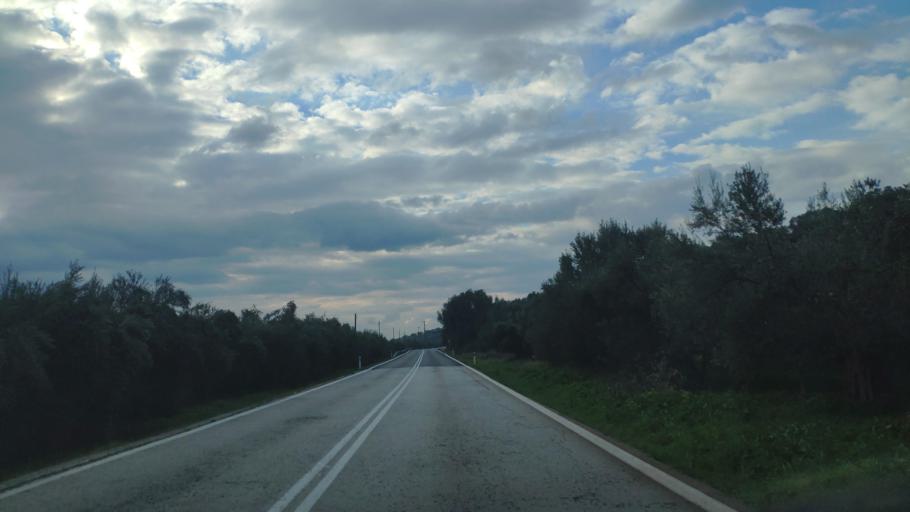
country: GR
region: Peloponnese
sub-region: Nomos Argolidos
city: Koutsopodi
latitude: 37.7468
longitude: 22.7342
